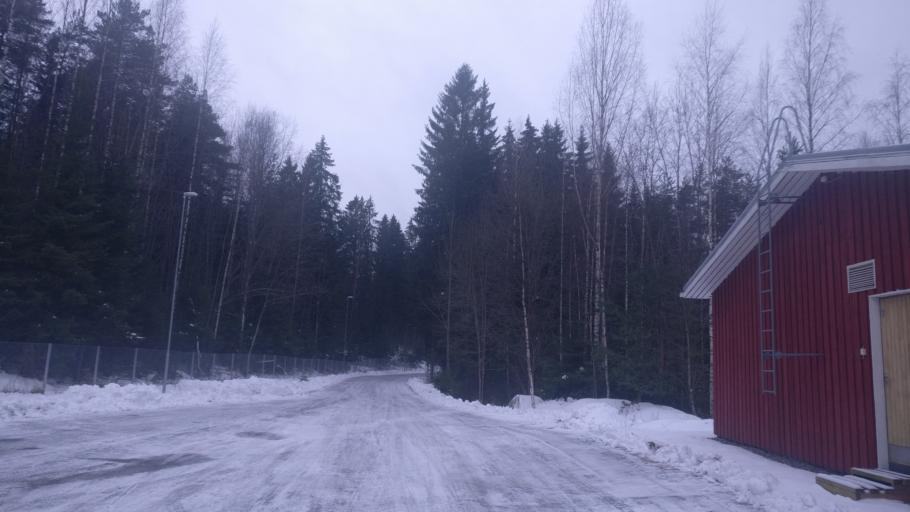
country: FI
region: Paijanne Tavastia
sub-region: Lahti
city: Lahti
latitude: 60.9662
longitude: 25.7433
